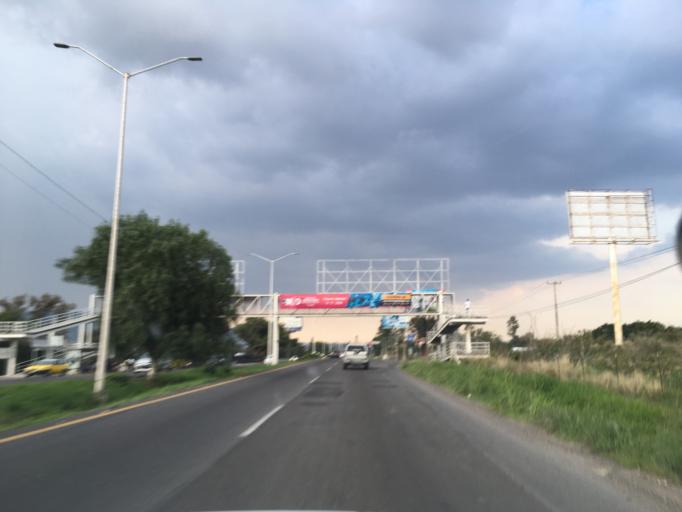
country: MX
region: Jalisco
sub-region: Tlajomulco de Zuniga
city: Lomas de San Agustin
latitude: 20.5236
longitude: -103.4806
